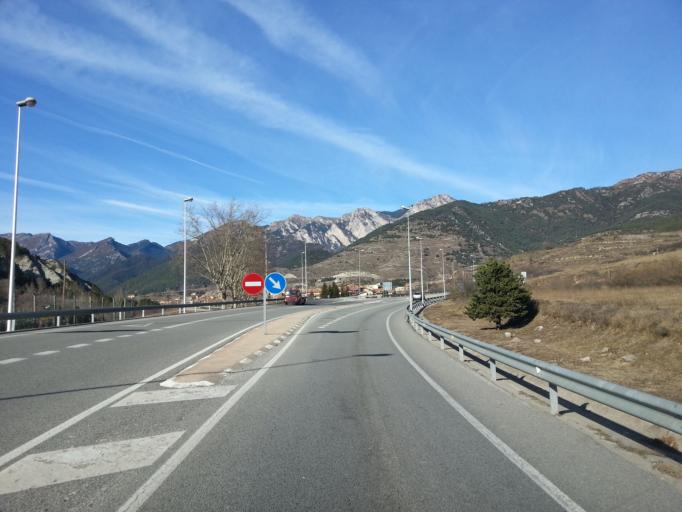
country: ES
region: Catalonia
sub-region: Provincia de Barcelona
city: Baga
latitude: 42.2453
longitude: 1.8697
